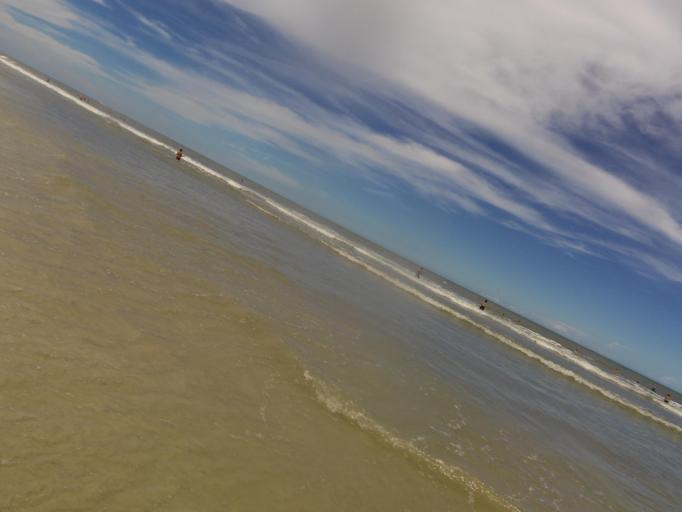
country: US
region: Florida
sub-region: Saint Johns County
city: Saint Augustine Beach
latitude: 29.8341
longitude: -81.2631
